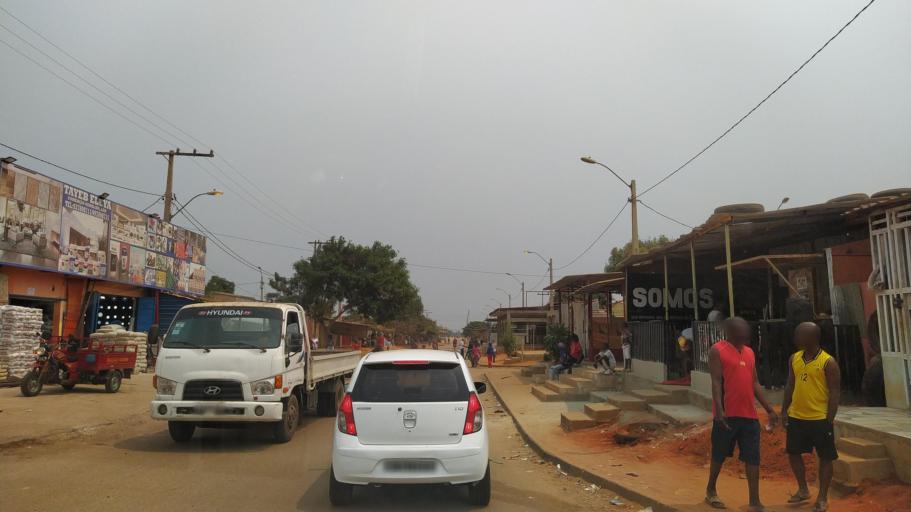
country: AO
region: Luanda
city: Luanda
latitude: -9.0729
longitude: 13.4048
